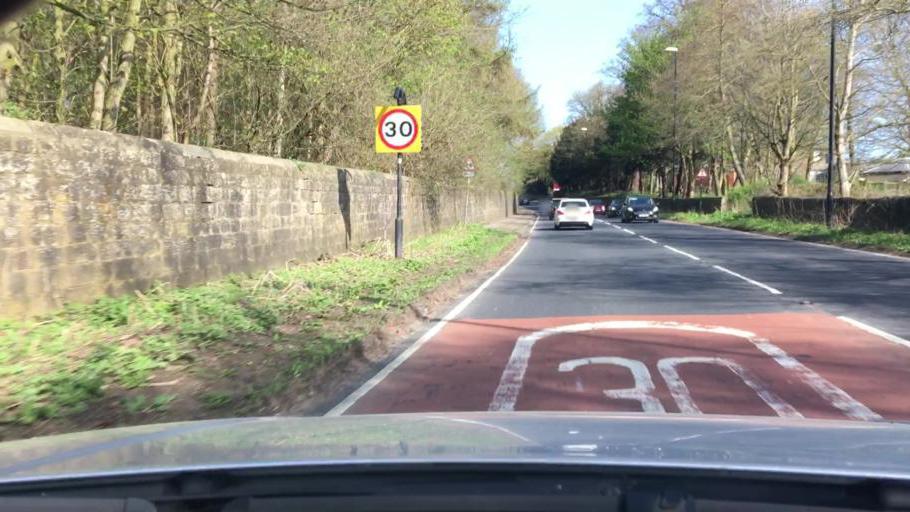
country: GB
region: England
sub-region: City and Borough of Leeds
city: Shadwell
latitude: 53.8974
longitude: -1.5106
